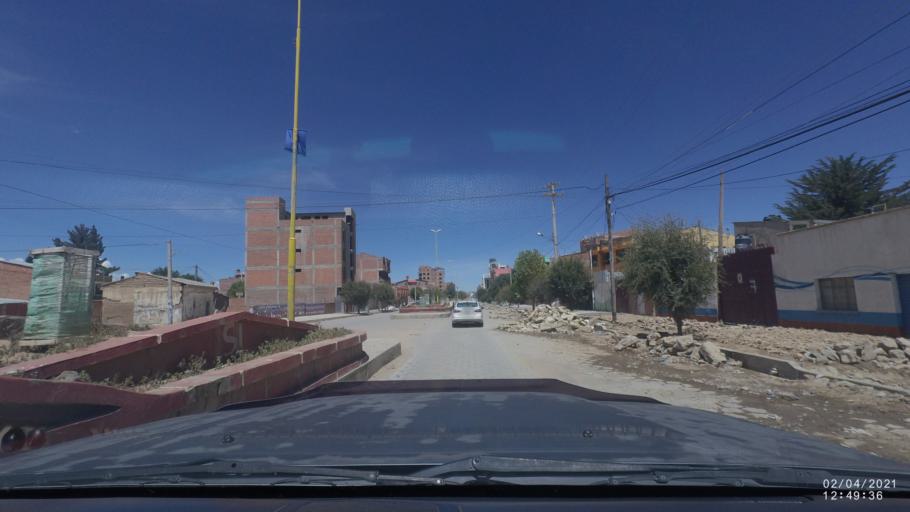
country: BO
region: Oruro
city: Oruro
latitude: -17.9726
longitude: -67.1384
